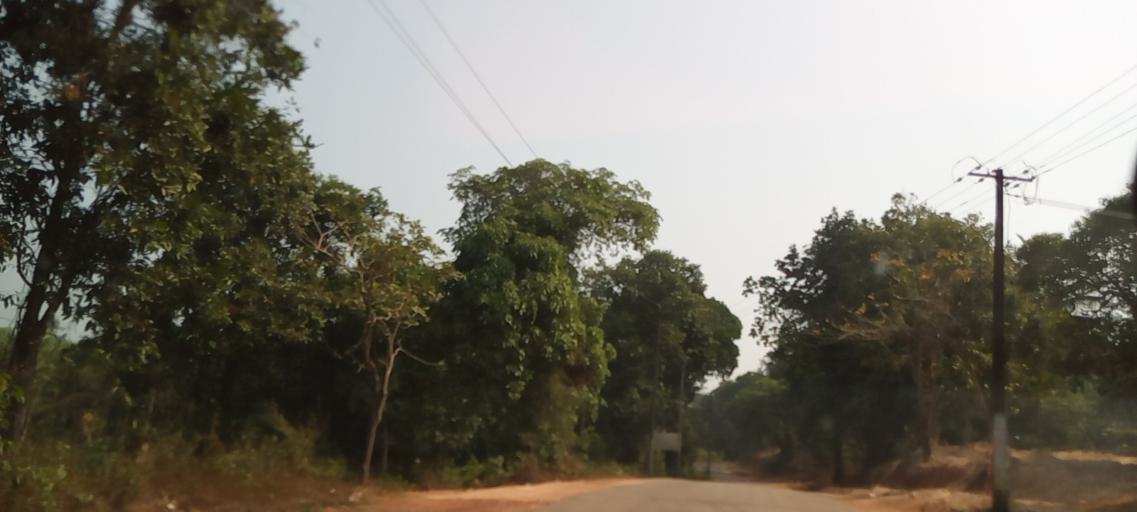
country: IN
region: Karnataka
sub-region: Udupi
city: Manipala
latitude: 13.5135
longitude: 74.8415
